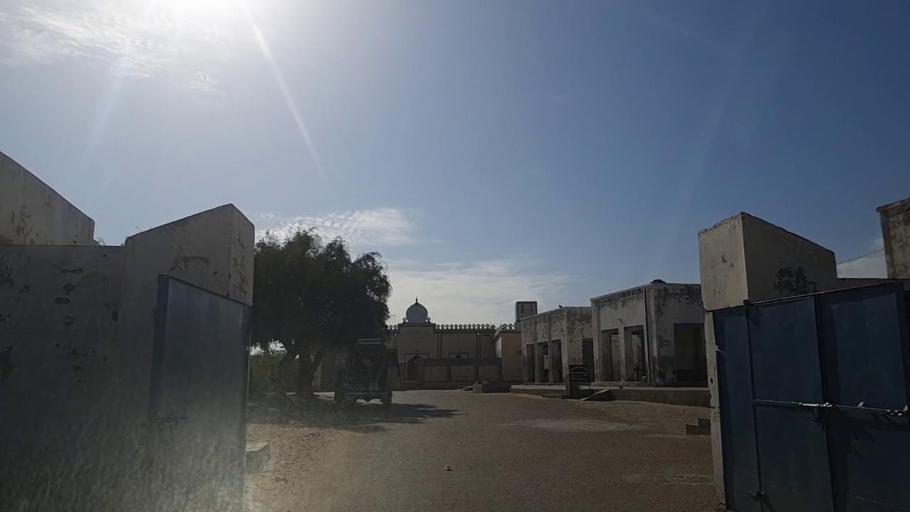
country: PK
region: Sindh
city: Naukot
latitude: 24.8413
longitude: 69.5402
